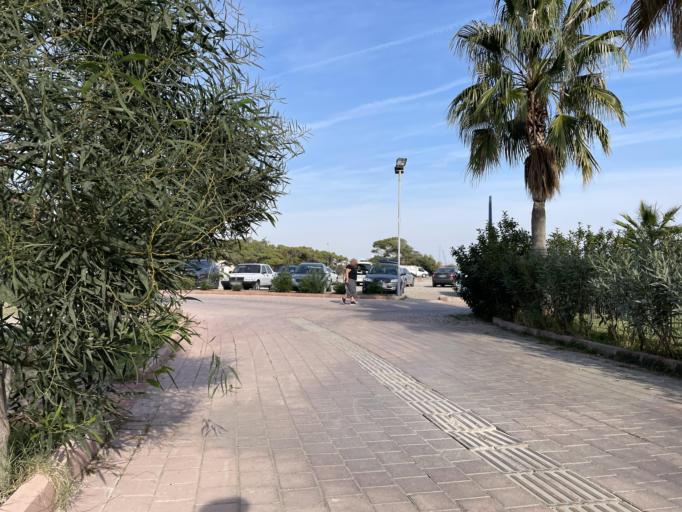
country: TR
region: Antalya
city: Cakirlar
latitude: 36.8285
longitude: 30.6008
